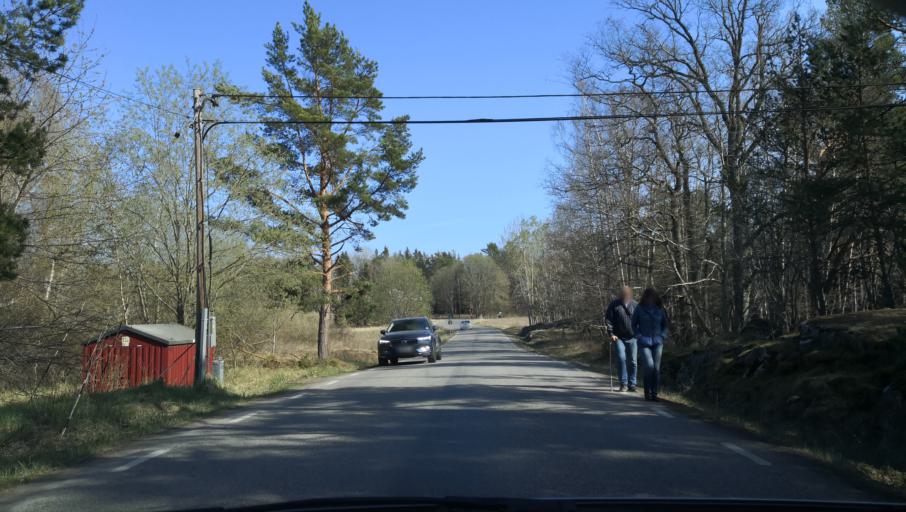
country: SE
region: Stockholm
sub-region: Varmdo Kommun
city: Holo
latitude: 59.3031
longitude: 18.6407
